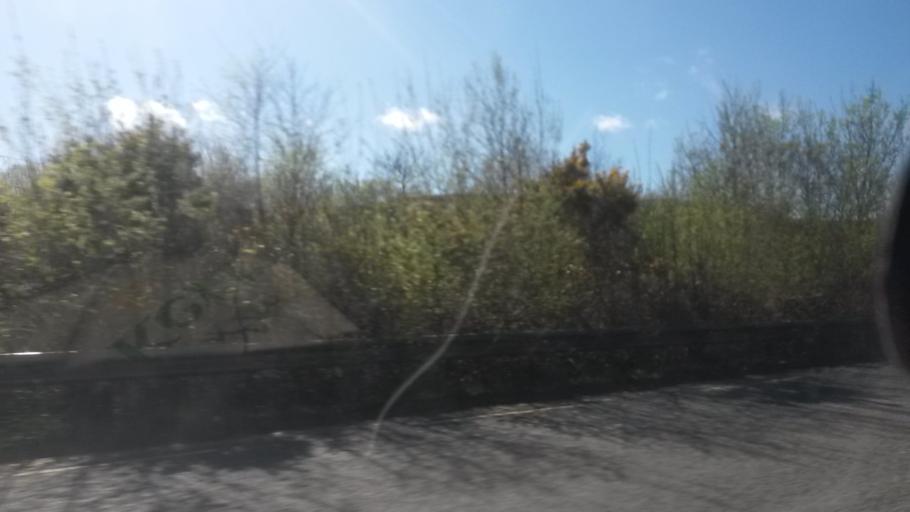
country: IE
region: Munster
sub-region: Ciarrai
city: Cill Airne
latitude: 51.9166
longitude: -9.3920
